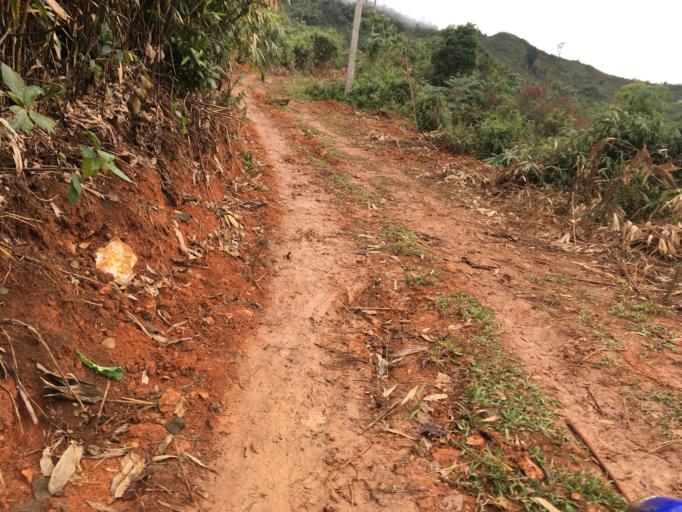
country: LA
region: Houaphan
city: Xamtay
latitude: 19.9018
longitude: 104.4601
